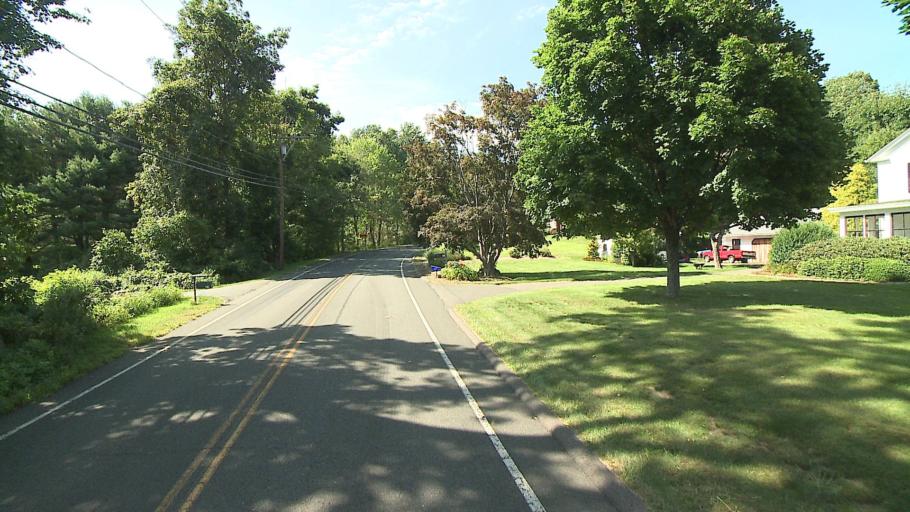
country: US
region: Connecticut
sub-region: Hartford County
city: West Simsbury
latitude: 41.8807
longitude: -72.8695
